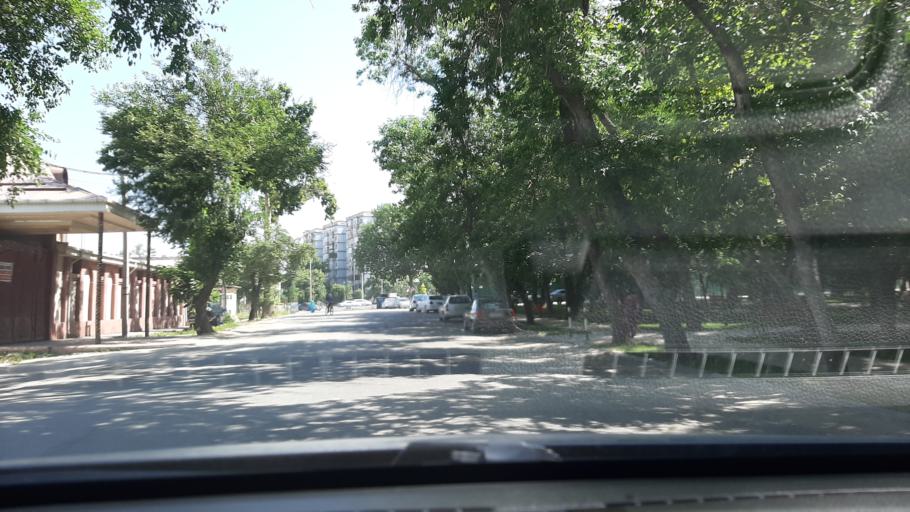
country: TJ
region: Dushanbe
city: Dushanbe
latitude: 38.5571
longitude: 68.7573
